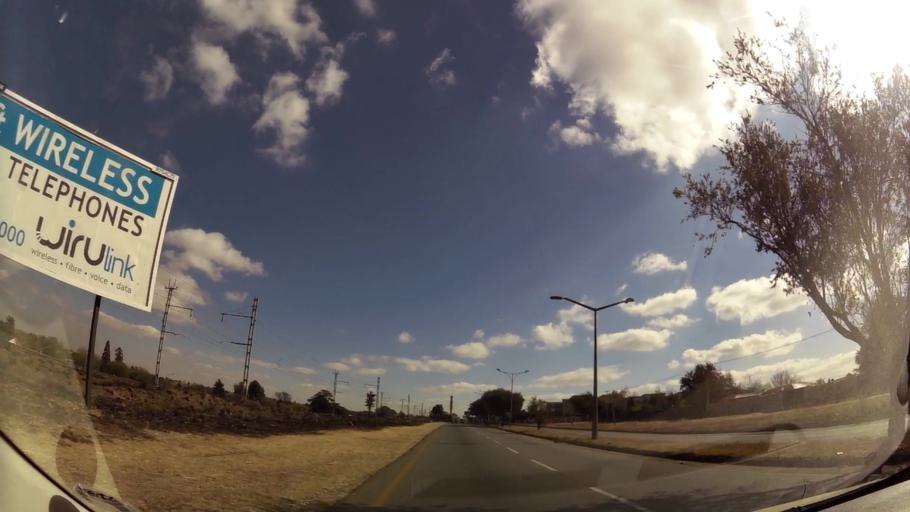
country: ZA
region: Gauteng
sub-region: City of Johannesburg Metropolitan Municipality
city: Roodepoort
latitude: -26.1252
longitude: 27.8266
